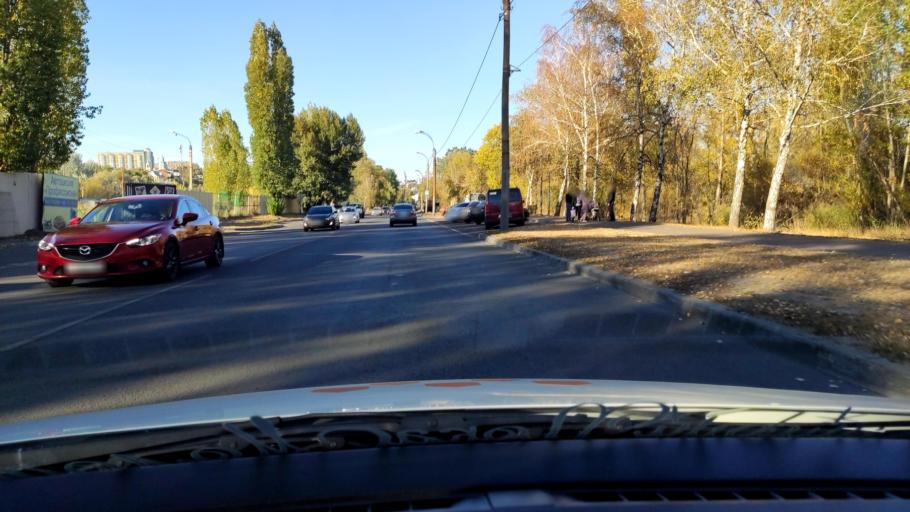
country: RU
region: Voronezj
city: Voronezh
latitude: 51.6456
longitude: 39.2112
